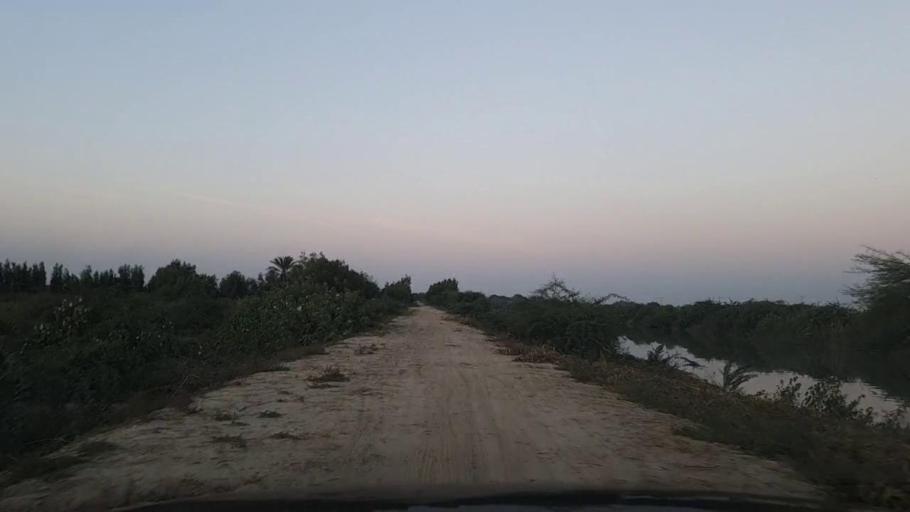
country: PK
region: Sindh
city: Thatta
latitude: 24.7408
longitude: 67.9567
